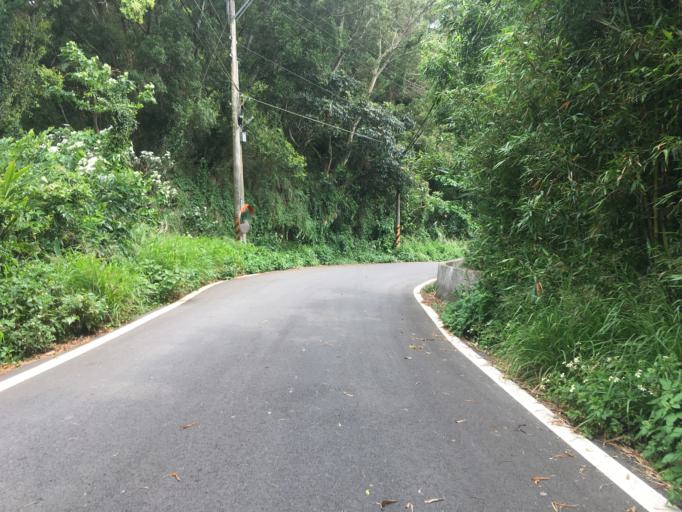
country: TW
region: Taiwan
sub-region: Hsinchu
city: Hsinchu
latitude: 24.7455
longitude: 120.9847
